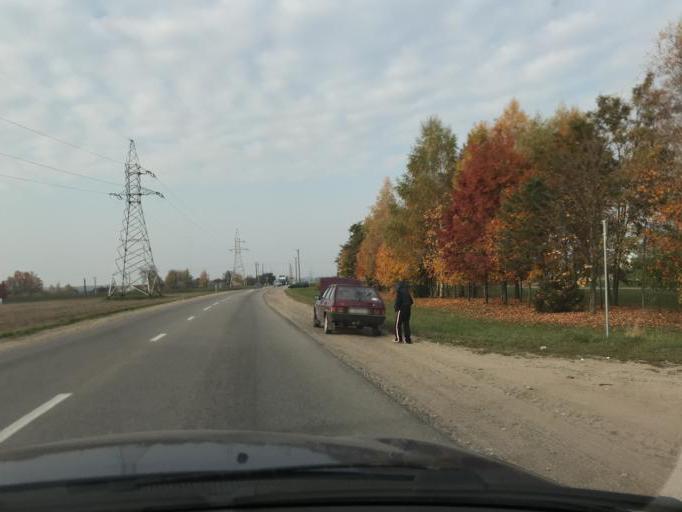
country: BY
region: Grodnenskaya
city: Lida
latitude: 53.8619
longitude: 25.2850
